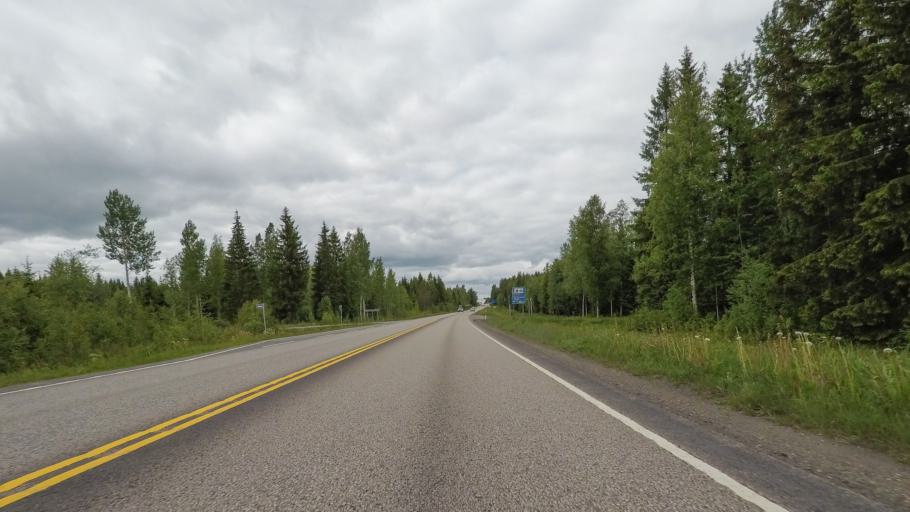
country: FI
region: Central Finland
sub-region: Joutsa
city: Joutsa
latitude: 61.7801
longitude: 26.0962
